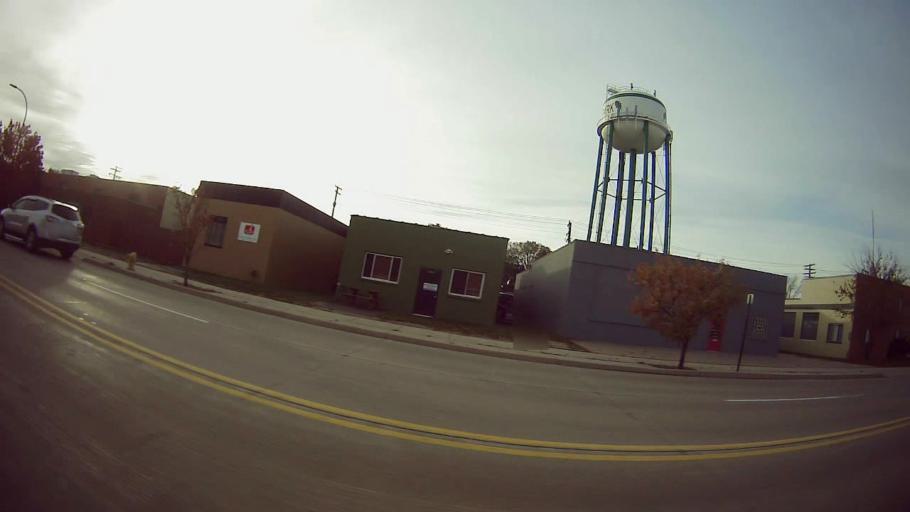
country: US
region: Michigan
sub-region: Oakland County
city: Berkley
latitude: 42.4887
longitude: -83.1946
